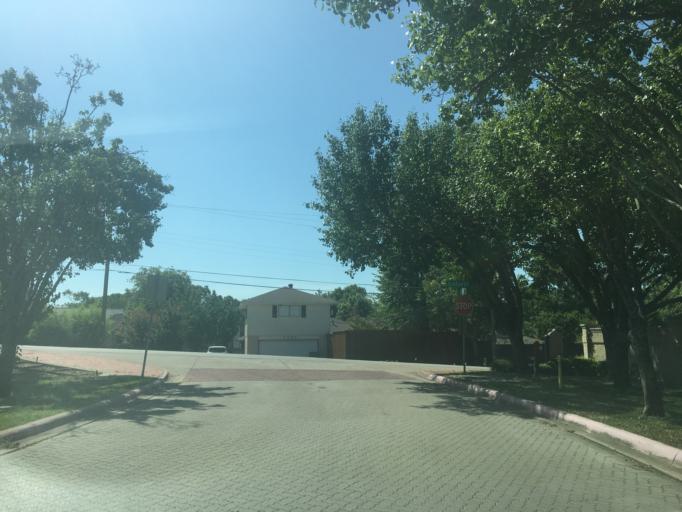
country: US
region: Texas
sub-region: Dallas County
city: Highland Park
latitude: 32.8674
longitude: -96.7306
